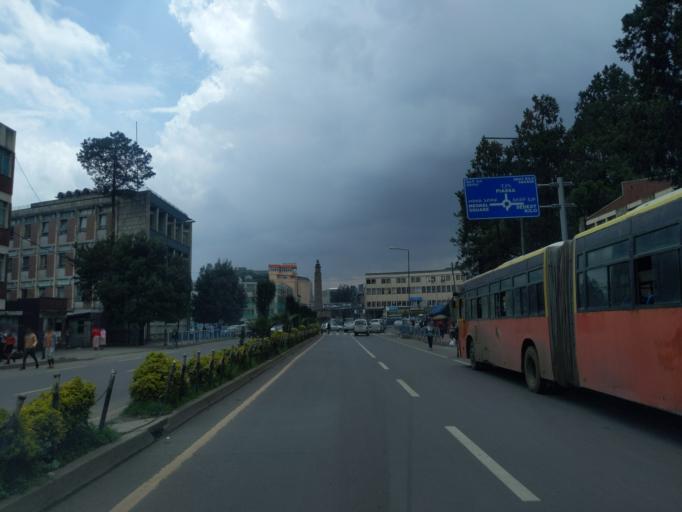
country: ET
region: Adis Abeba
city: Addis Ababa
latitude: 9.0325
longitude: 38.7644
